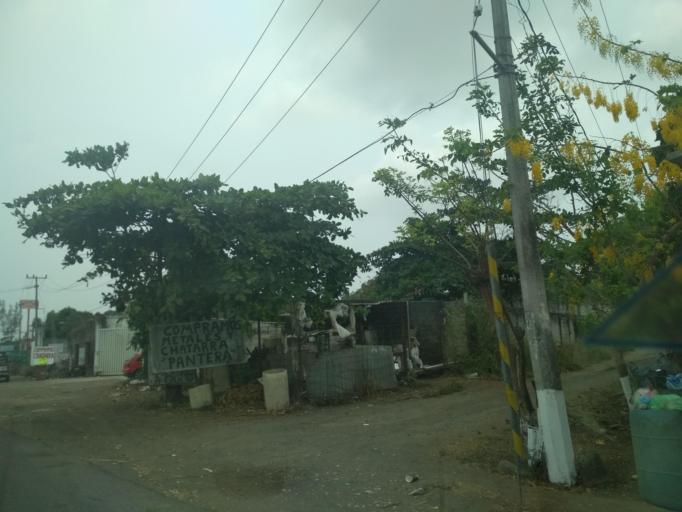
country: MX
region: Veracruz
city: Paso del Toro
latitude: 19.0260
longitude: -96.1384
